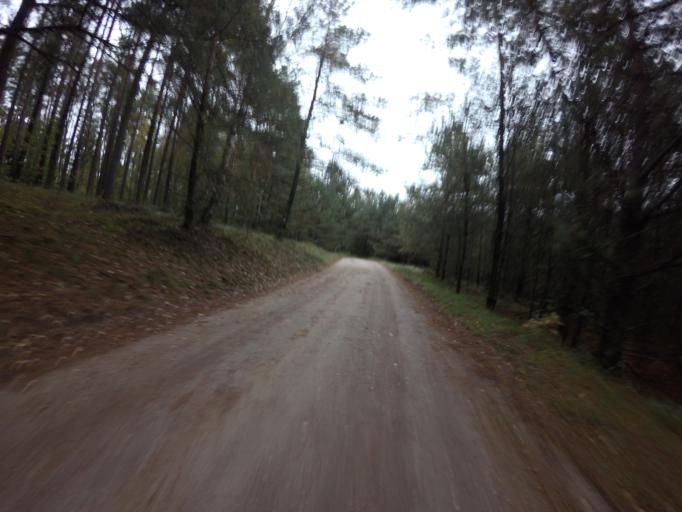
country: PL
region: Pomeranian Voivodeship
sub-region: Powiat kartuski
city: Stezyca
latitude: 54.1610
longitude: 17.9223
